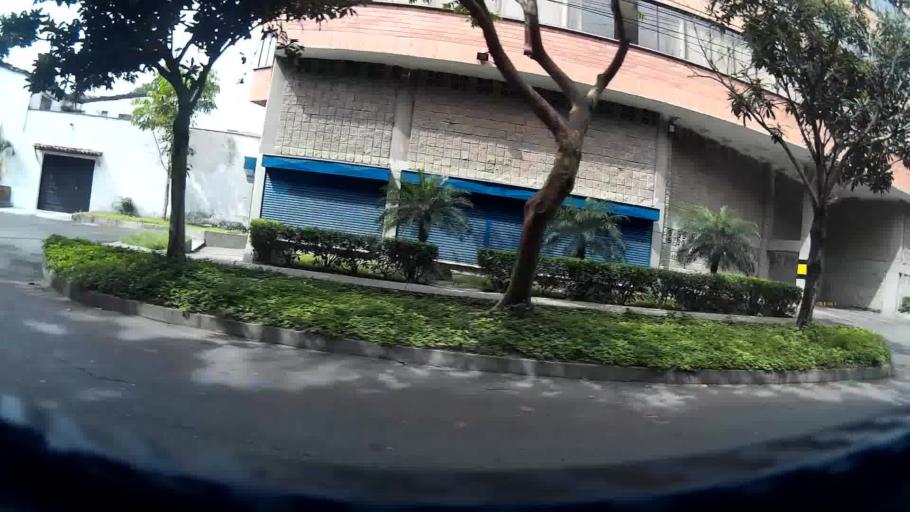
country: CO
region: Antioquia
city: Medellin
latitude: 6.2598
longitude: -75.6028
